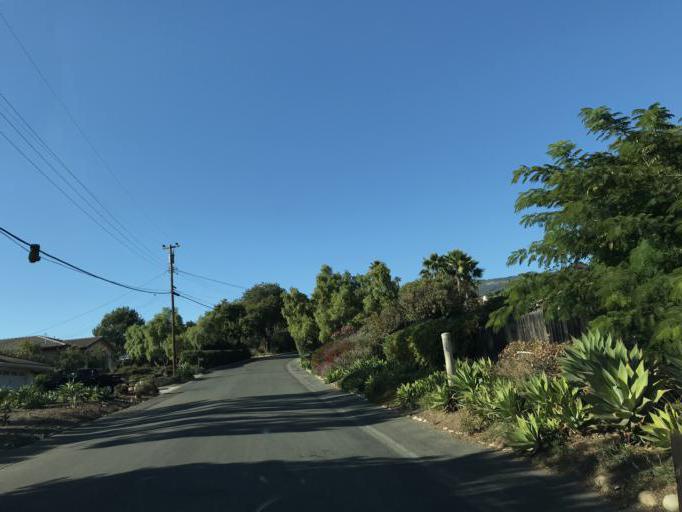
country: US
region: California
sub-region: Santa Barbara County
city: Goleta
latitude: 34.4593
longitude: -119.8203
